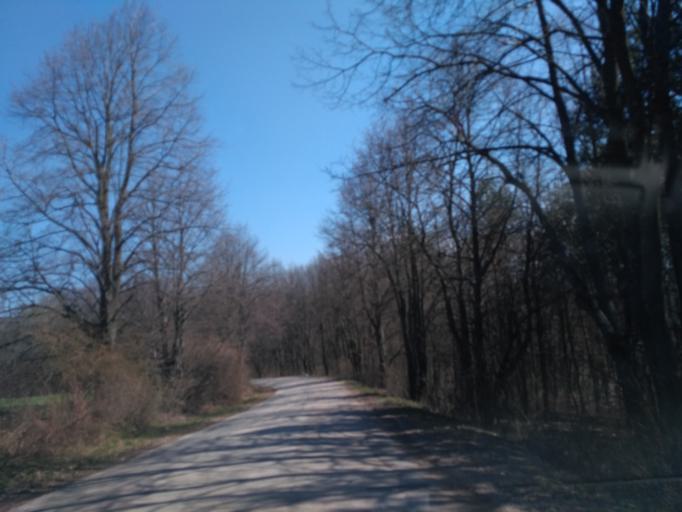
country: SK
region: Kosicky
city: Moldava nad Bodvou
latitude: 48.6499
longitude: 20.9940
